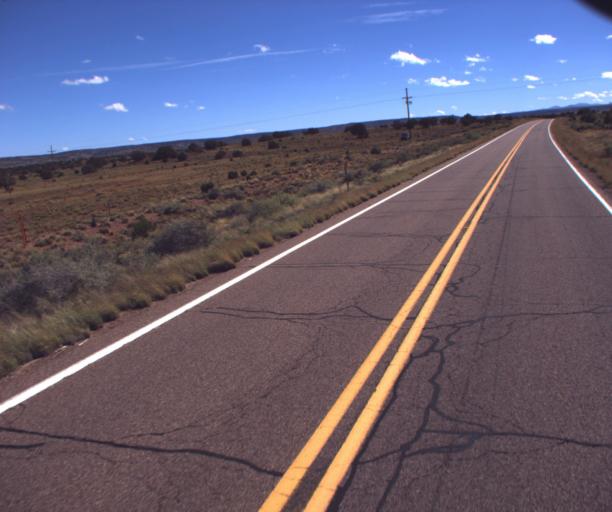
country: US
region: Arizona
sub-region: Apache County
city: Saint Johns
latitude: 34.5375
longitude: -109.6208
